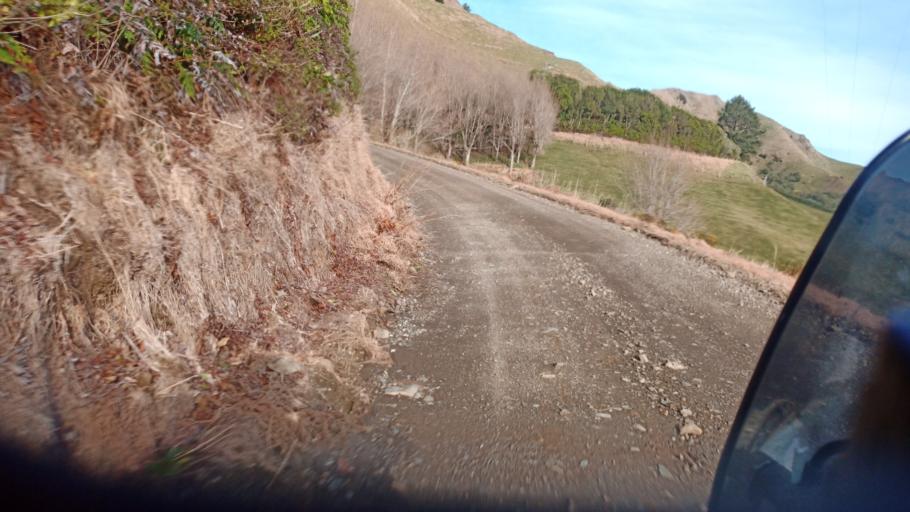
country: NZ
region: Gisborne
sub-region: Gisborne District
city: Gisborne
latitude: -38.4537
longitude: 177.5382
